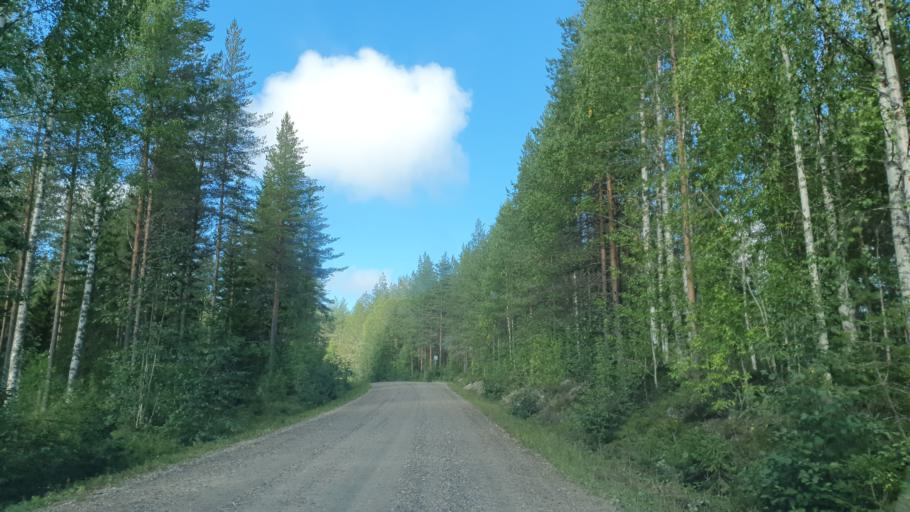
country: FI
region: Kainuu
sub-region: Kehys-Kainuu
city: Kuhmo
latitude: 64.0379
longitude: 29.1455
